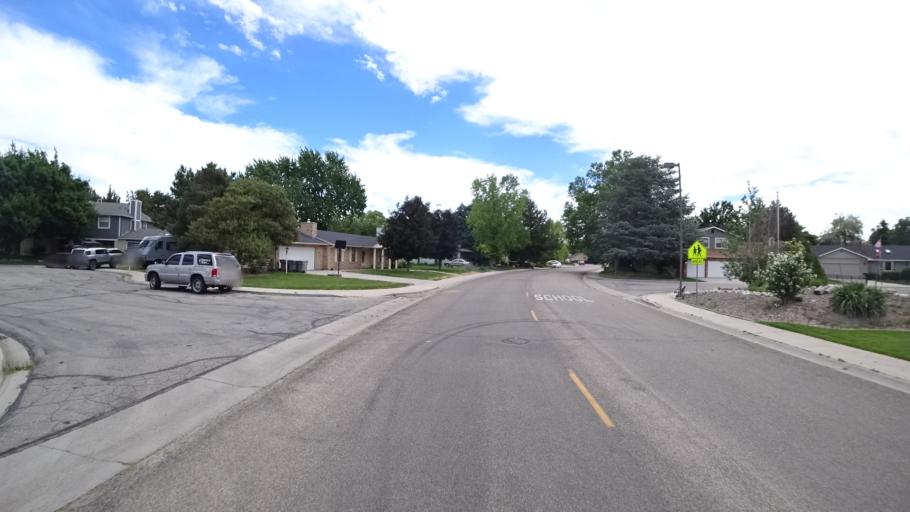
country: US
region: Idaho
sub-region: Ada County
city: Eagle
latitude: 43.6419
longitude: -116.3327
